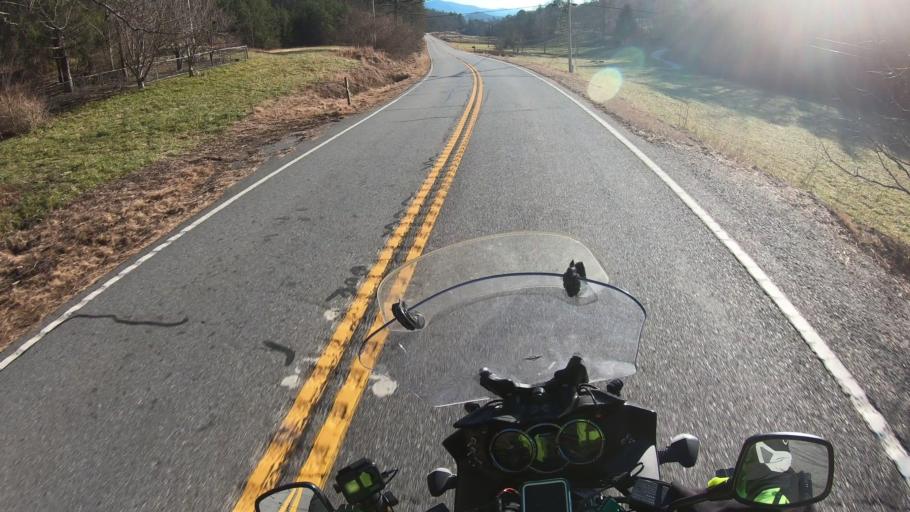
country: US
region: Georgia
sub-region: Fannin County
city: Blue Ridge
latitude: 34.7910
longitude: -84.1821
